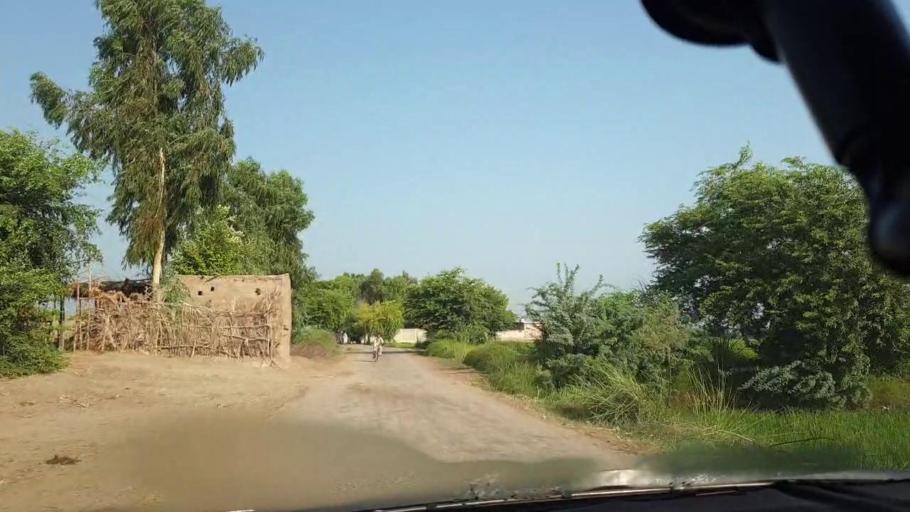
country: PK
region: Sindh
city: Larkana
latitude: 27.6183
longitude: 68.2164
